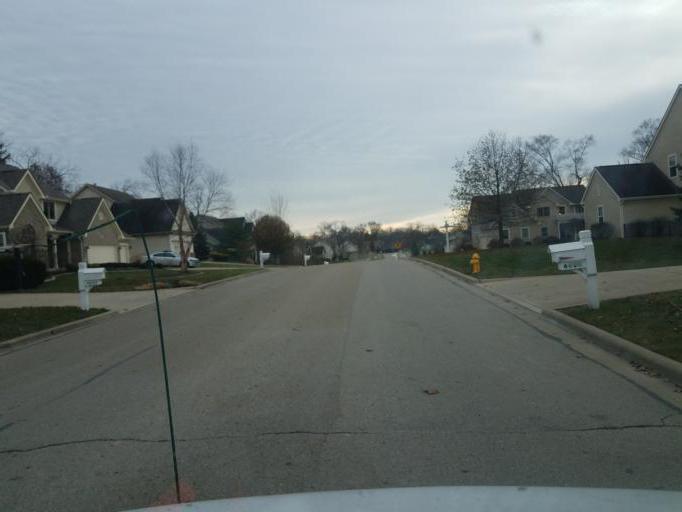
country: US
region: Ohio
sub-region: Franklin County
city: Westerville
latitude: 40.1770
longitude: -82.9416
